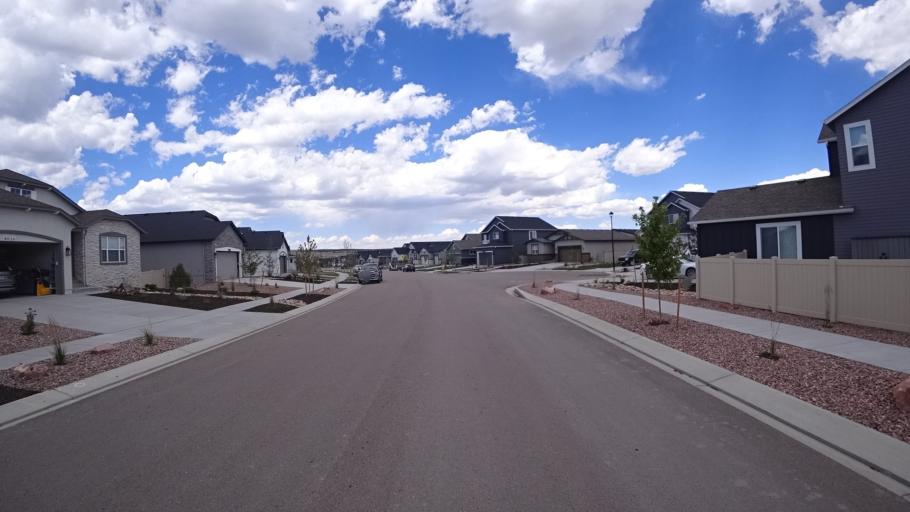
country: US
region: Colorado
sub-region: El Paso County
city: Black Forest
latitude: 38.9472
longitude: -104.7073
